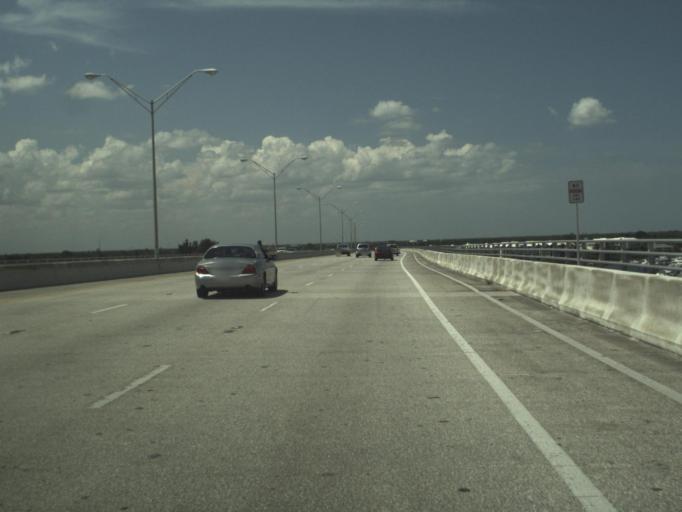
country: US
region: Florida
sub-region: Martin County
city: Stuart
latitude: 27.2062
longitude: -80.2587
